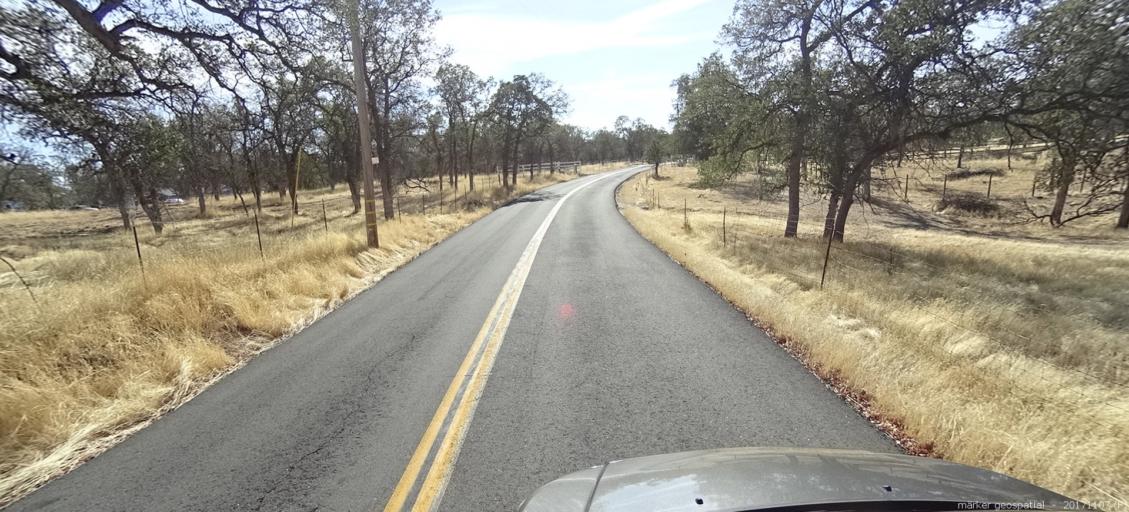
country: US
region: California
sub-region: Shasta County
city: Shasta
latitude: 40.4414
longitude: -122.5270
